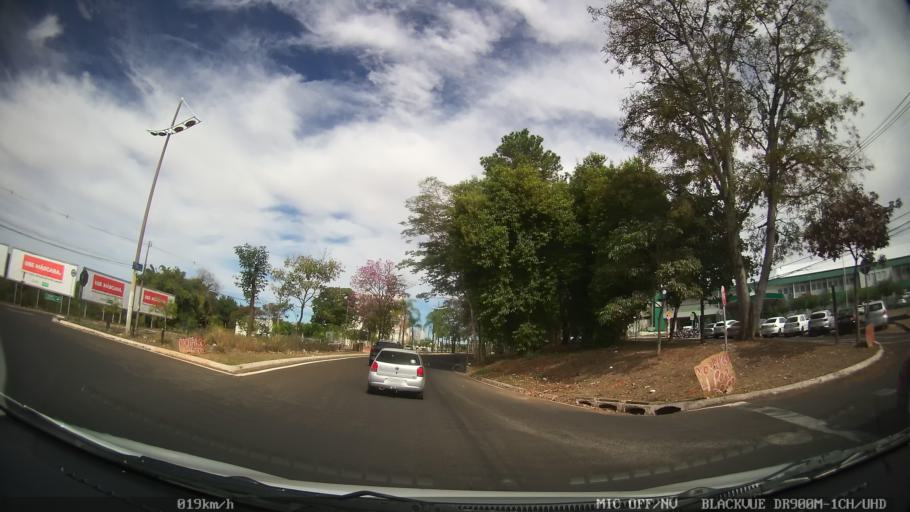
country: BR
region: Sao Paulo
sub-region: Catanduva
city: Catanduva
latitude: -21.1566
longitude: -48.9843
